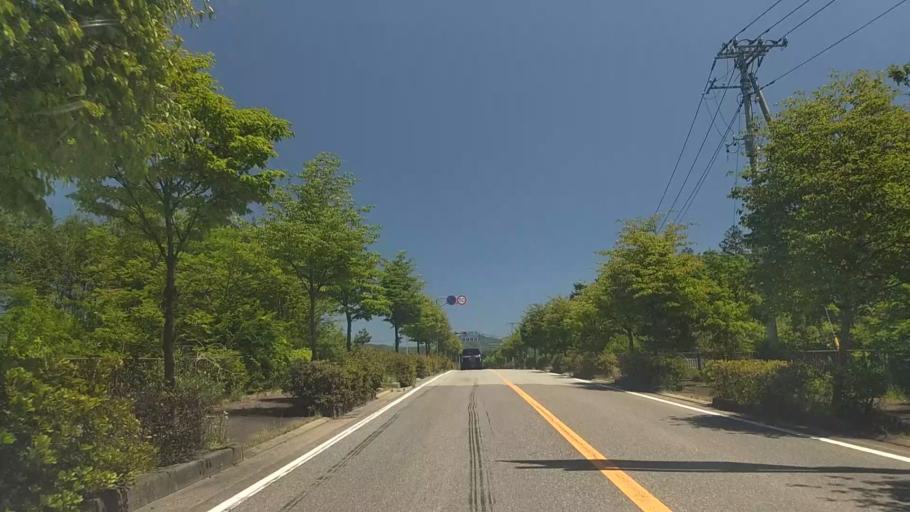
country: JP
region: Yamanashi
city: Nirasaki
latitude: 35.8390
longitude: 138.4316
